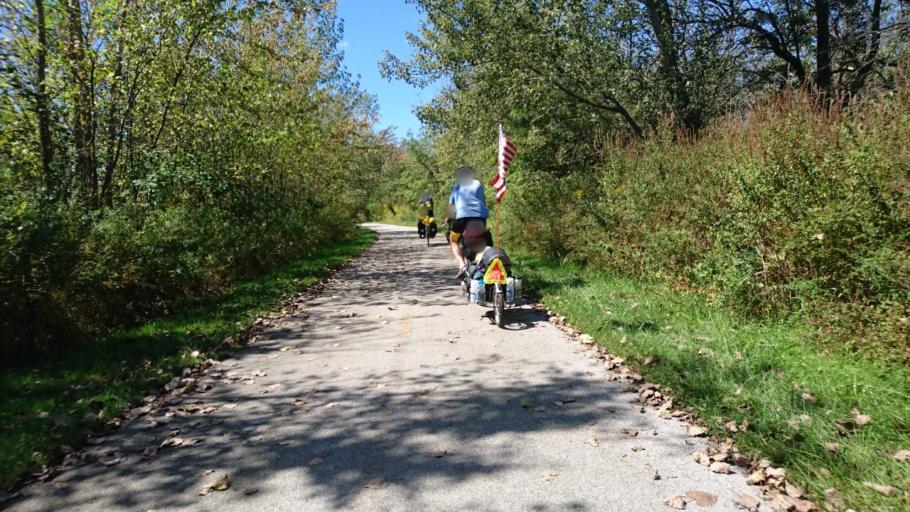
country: US
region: Illinois
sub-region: Cook County
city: Lansing
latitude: 41.5477
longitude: -87.5647
